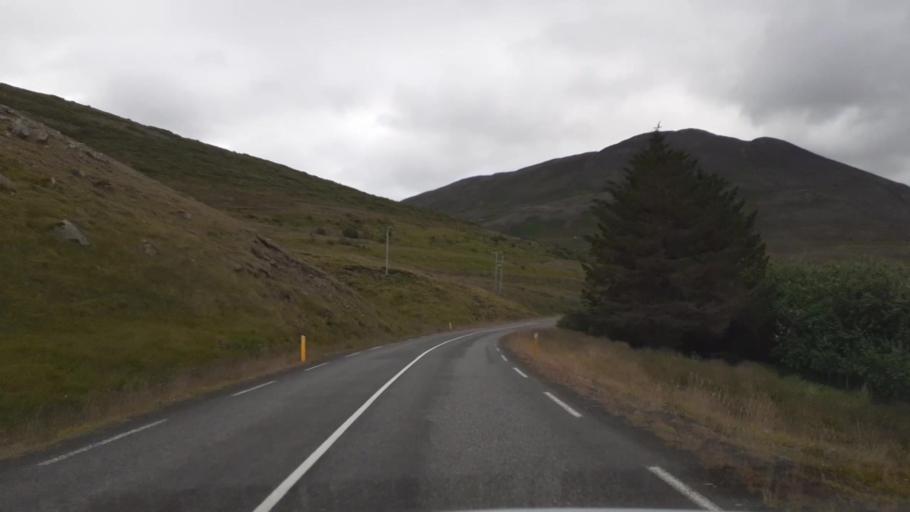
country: IS
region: Northeast
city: Akureyri
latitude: 65.8231
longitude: -18.0522
